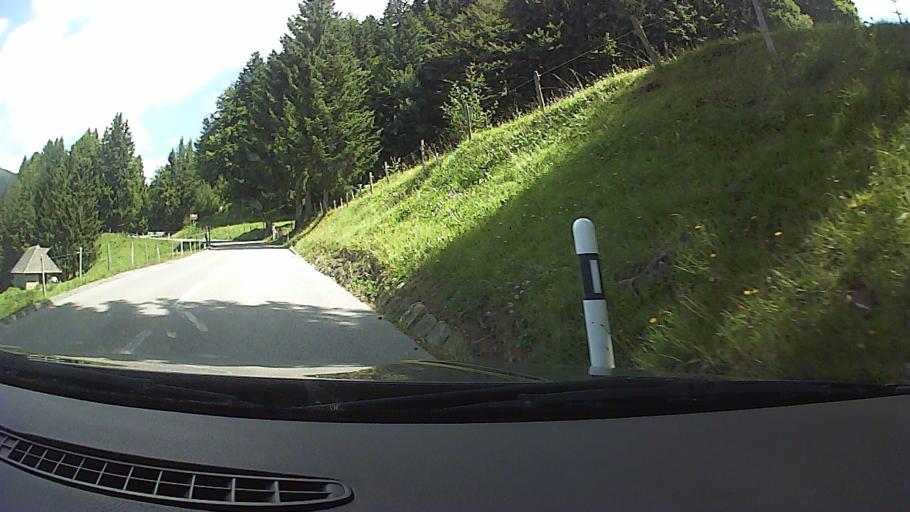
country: CH
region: Fribourg
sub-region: Veveyse District
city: Chatel-Saint-Denis
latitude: 46.5233
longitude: 6.9351
